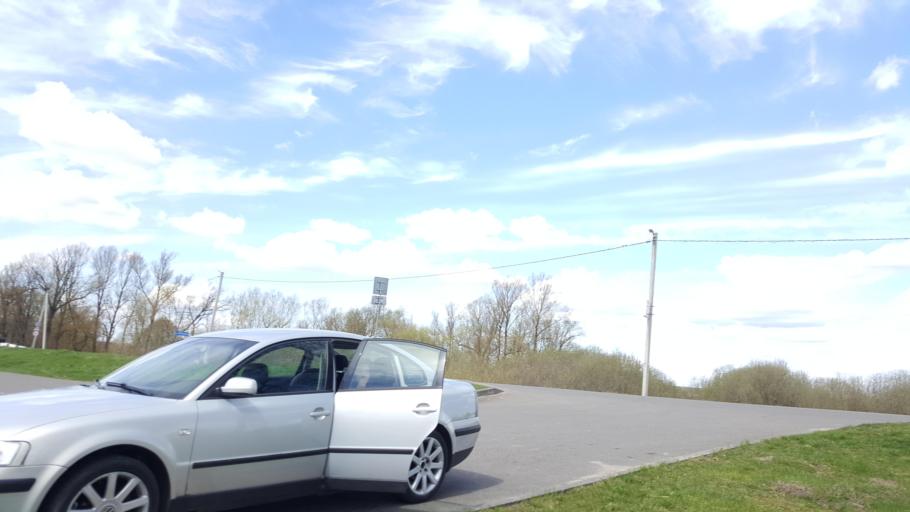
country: BY
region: Brest
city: Kamyanyets
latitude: 52.4016
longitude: 23.8055
